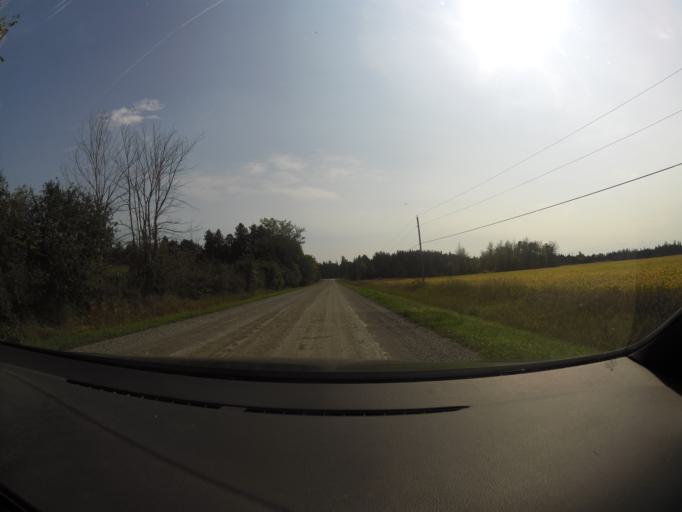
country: CA
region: Ontario
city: Carleton Place
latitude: 45.3274
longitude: -76.1769
